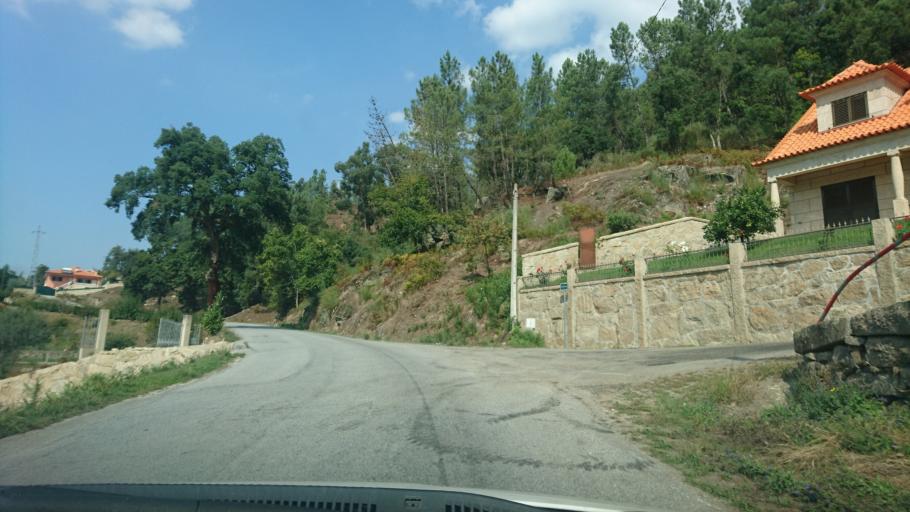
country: PT
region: Vila Real
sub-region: Mondim de Basto
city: Mondim de Basto
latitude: 41.4177
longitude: -7.9369
